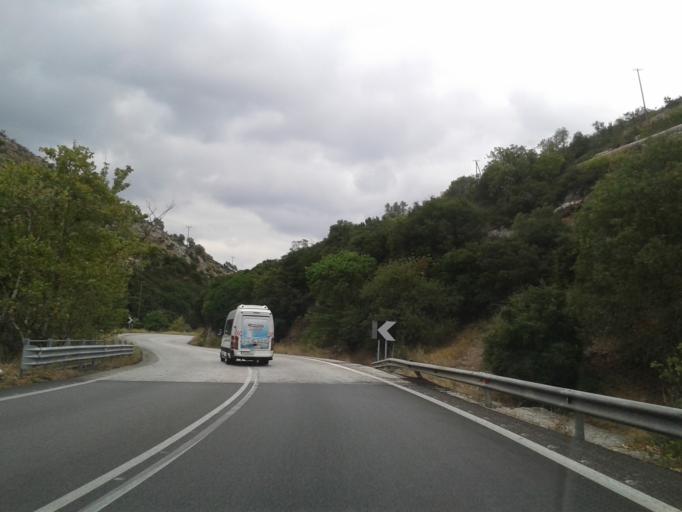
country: GR
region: Peloponnese
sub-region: Nomos Korinthias
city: Nemea
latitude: 37.7880
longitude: 22.7225
